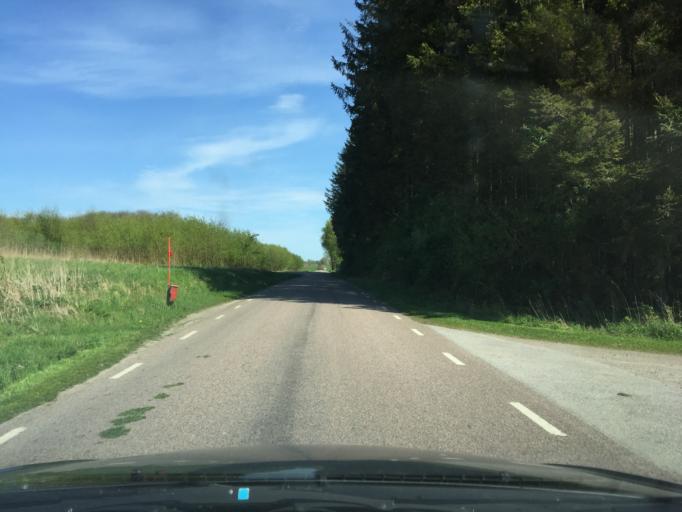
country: SE
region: Skane
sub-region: Sjobo Kommun
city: Blentarp
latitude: 55.5582
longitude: 13.5337
